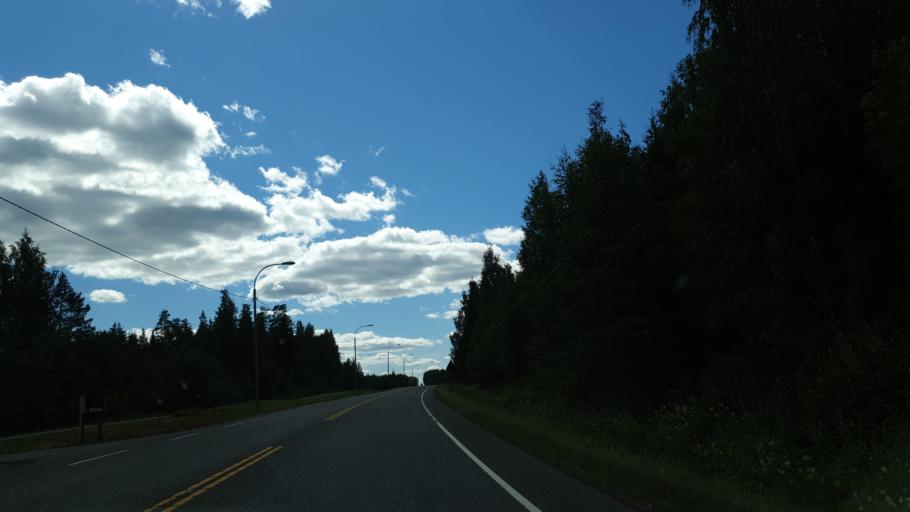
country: FI
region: Northern Savo
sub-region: Kuopio
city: Siilinjaervi
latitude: 63.1161
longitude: 27.7669
